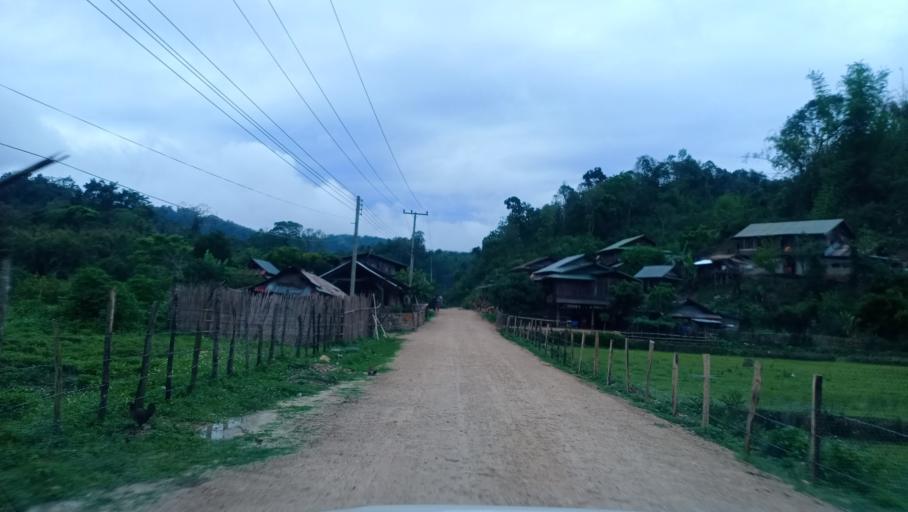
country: LA
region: Phongsali
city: Khoa
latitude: 21.2572
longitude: 102.6975
